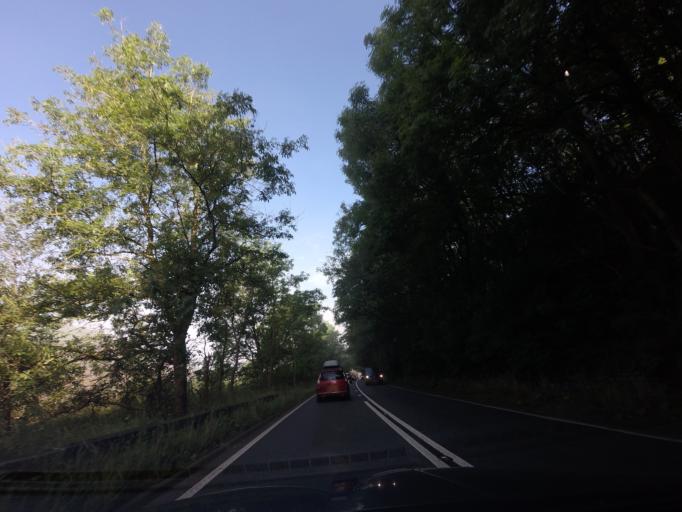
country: GB
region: England
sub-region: Derbyshire
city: Bakewell
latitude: 53.2418
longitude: -1.5767
